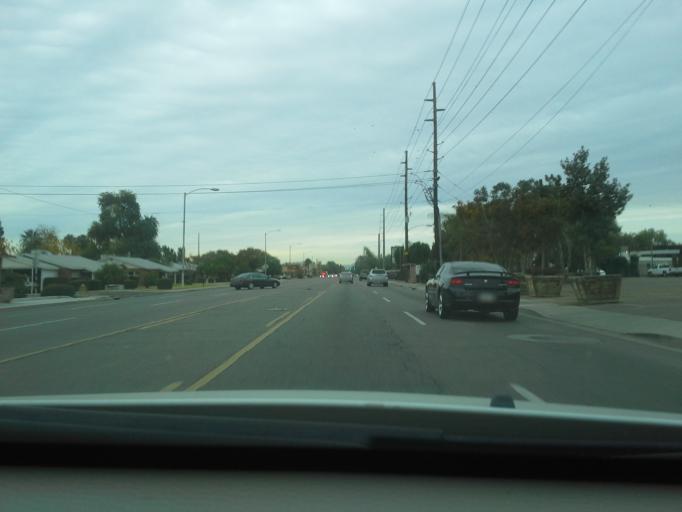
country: US
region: Arizona
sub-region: Maricopa County
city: Phoenix
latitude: 33.5383
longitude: -112.0601
